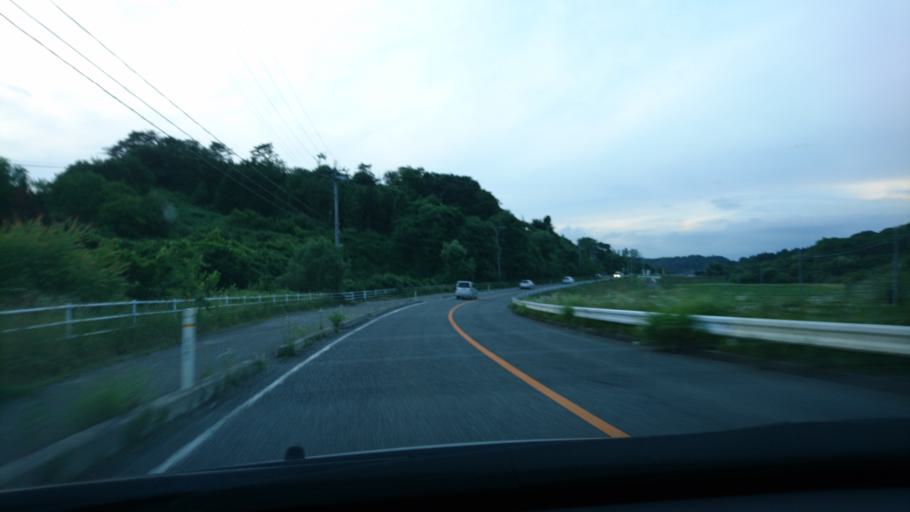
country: JP
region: Miyagi
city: Furukawa
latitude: 38.7588
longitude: 141.0041
